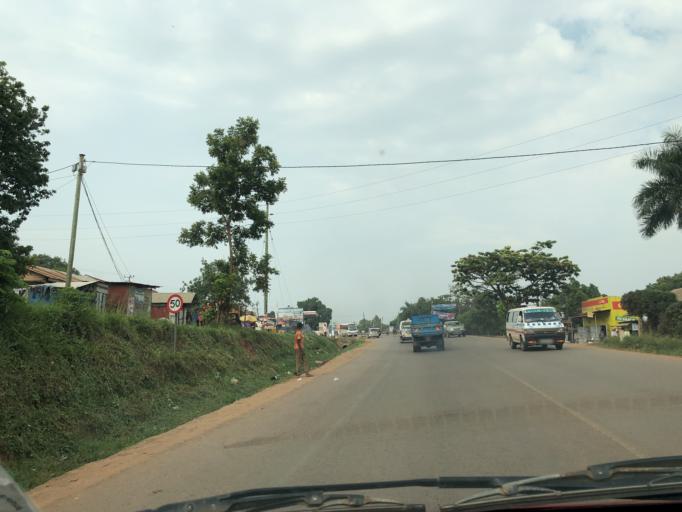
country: UG
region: Central Region
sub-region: Wakiso District
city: Kireka
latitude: 0.4096
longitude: 32.5944
